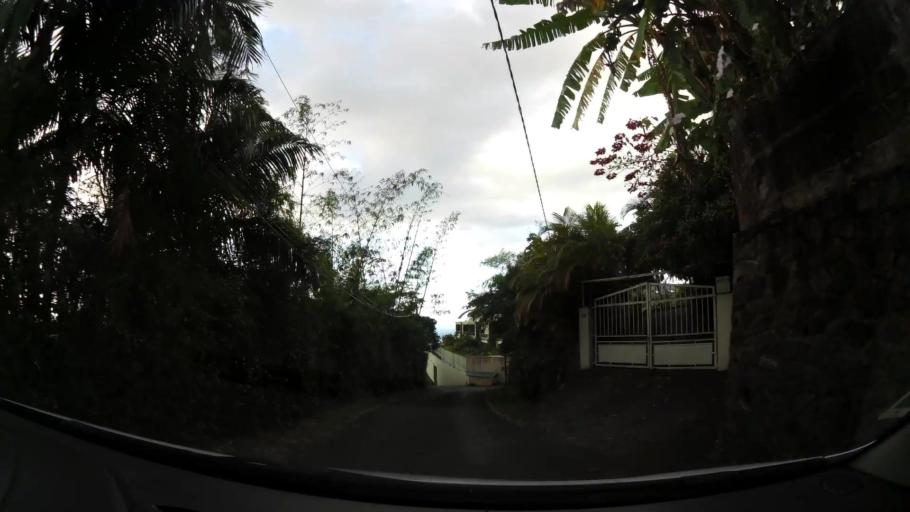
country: RE
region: Reunion
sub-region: Reunion
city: Saint-Denis
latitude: -20.9009
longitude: 55.4467
